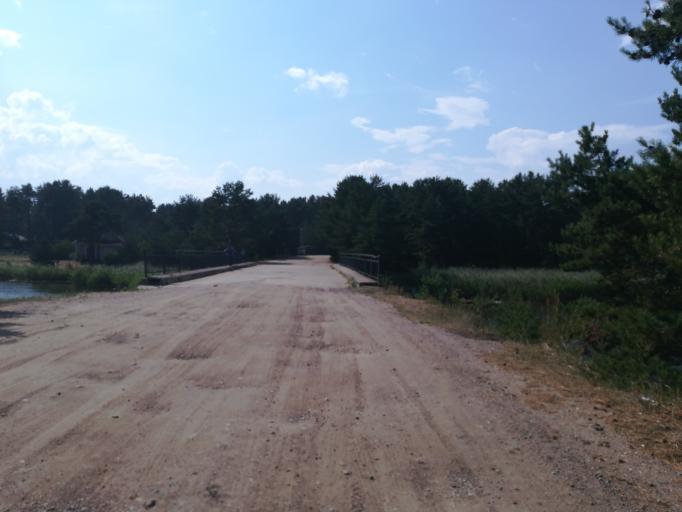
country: RU
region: Leningrad
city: Ust'-Luga
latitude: 59.7746
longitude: 28.1313
